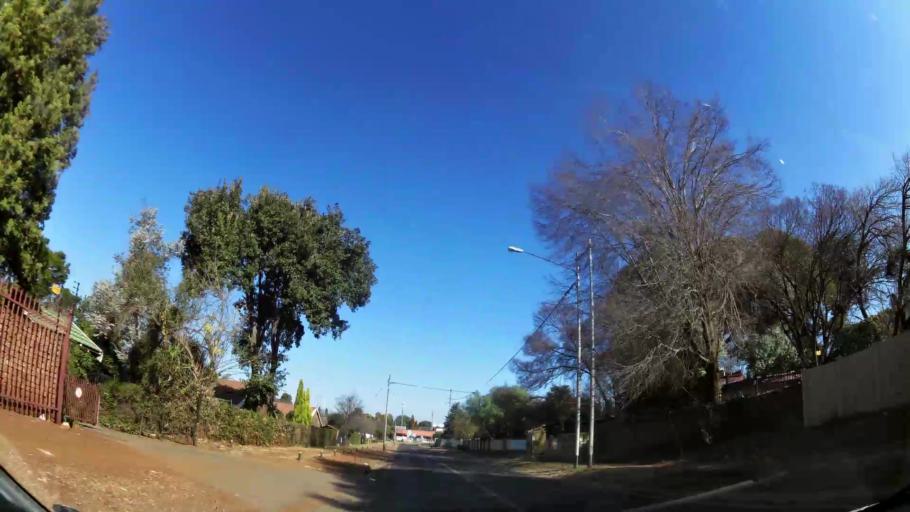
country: ZA
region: Gauteng
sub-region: City of Tshwane Metropolitan Municipality
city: Centurion
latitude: -25.8572
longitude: 28.1670
